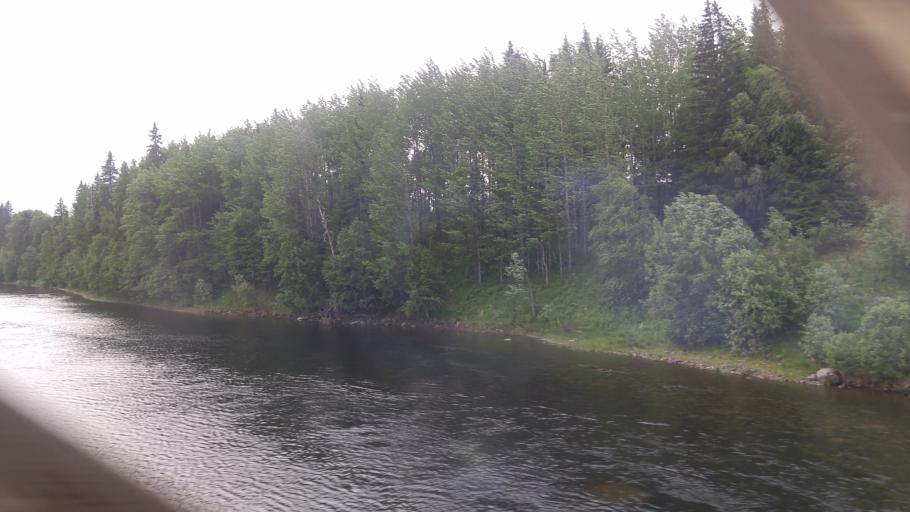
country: SE
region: Jaemtland
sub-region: Are Kommun
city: Are
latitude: 63.3885
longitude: 12.9024
